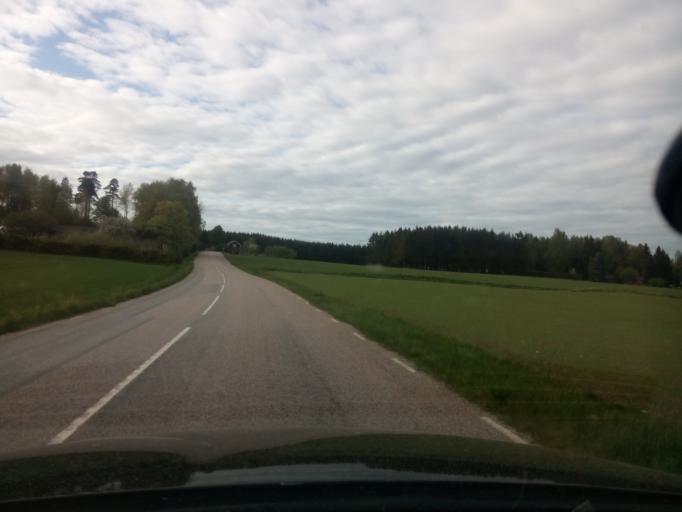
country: SE
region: Soedermanland
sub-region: Nykopings Kommun
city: Nykoping
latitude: 58.8387
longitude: 16.9362
